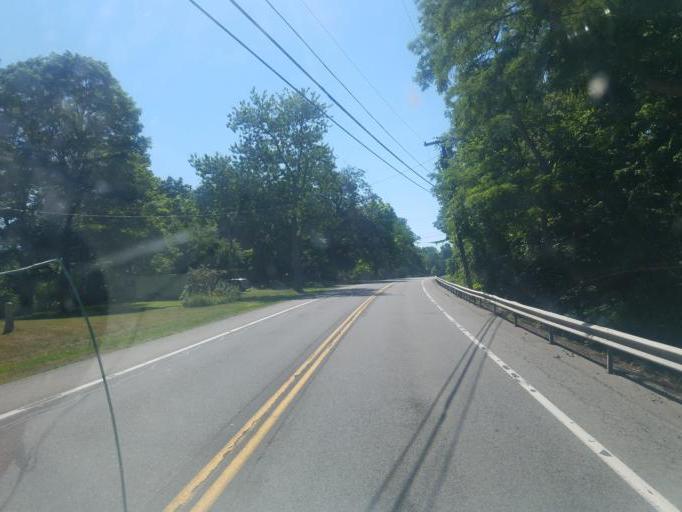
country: US
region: New York
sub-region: Ontario County
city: Phelps
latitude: 42.9511
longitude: -77.0333
